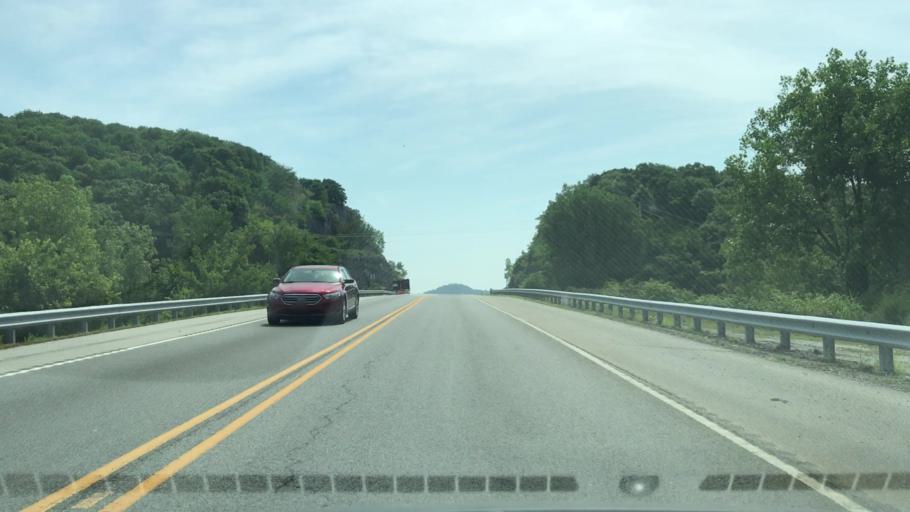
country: US
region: Tennessee
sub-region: Smith County
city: Carthage
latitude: 36.2595
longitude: -85.9477
